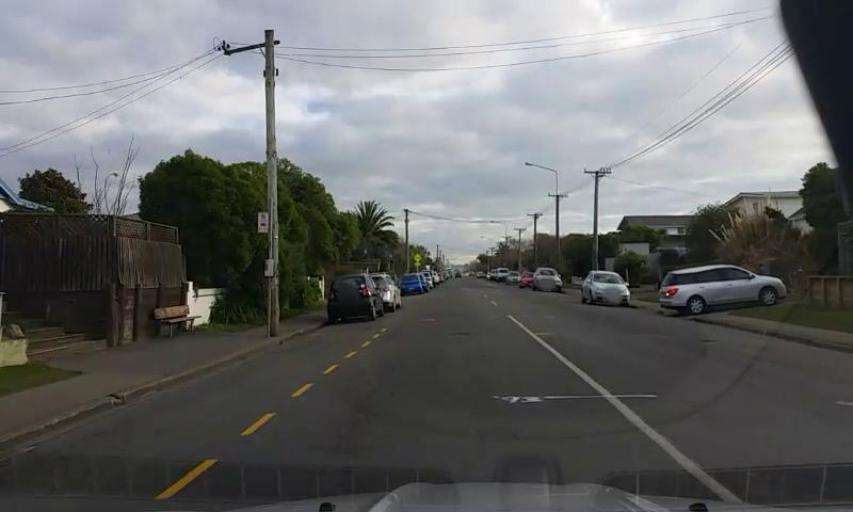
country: NZ
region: Canterbury
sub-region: Christchurch City
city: Christchurch
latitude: -43.5277
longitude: 172.7346
